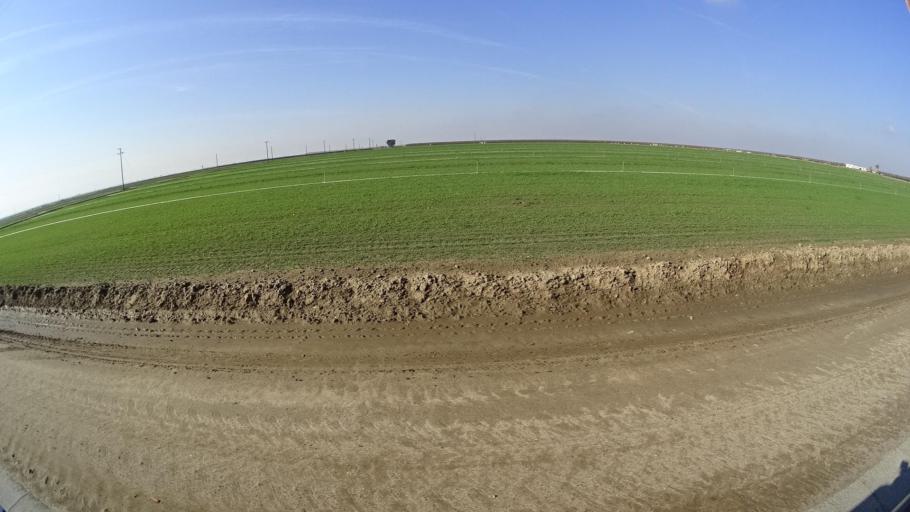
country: US
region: California
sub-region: Kern County
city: Arvin
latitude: 35.1952
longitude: -118.8782
